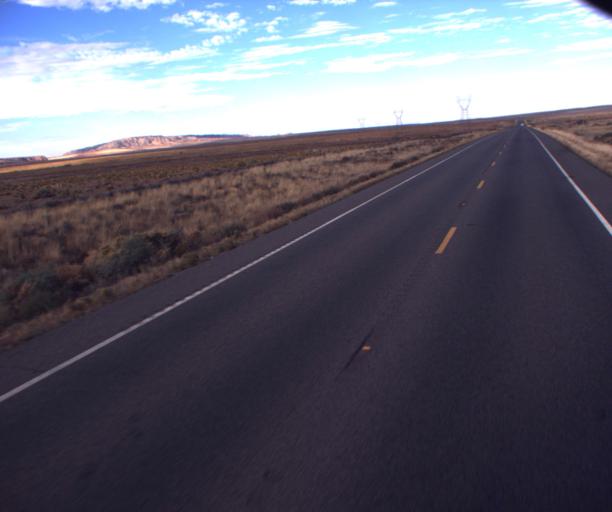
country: US
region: Arizona
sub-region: Apache County
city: Lukachukai
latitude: 36.9353
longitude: -109.2343
